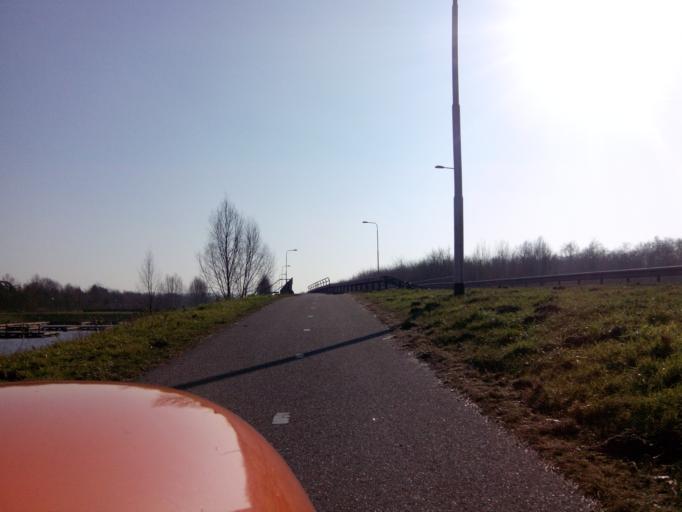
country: NL
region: Flevoland
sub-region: Gemeente Zeewolde
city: Zeewolde
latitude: 52.3368
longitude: 5.5113
